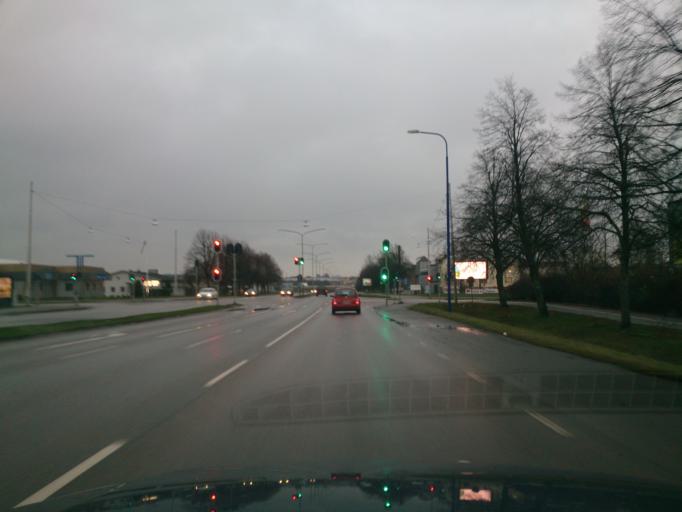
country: SE
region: OEstergoetland
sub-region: Norrkopings Kommun
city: Norrkoping
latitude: 58.6026
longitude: 16.1861
